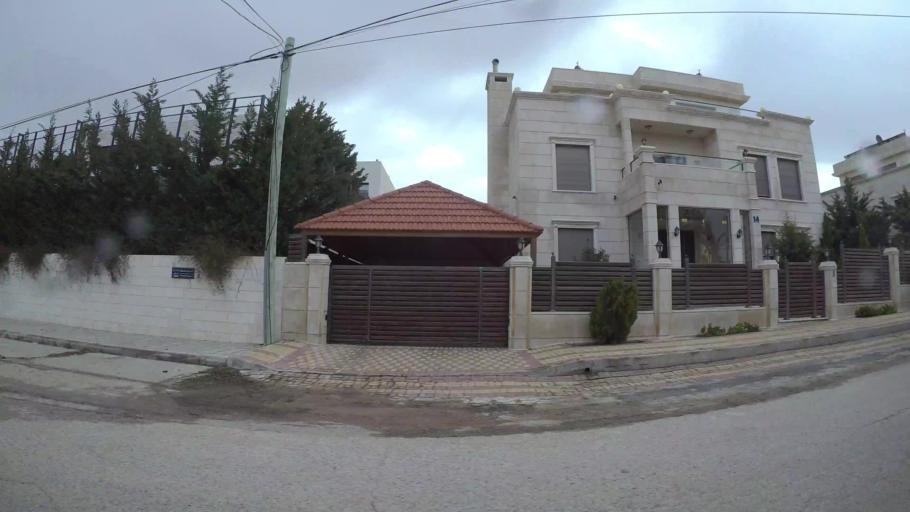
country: JO
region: Amman
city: Wadi as Sir
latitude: 31.9865
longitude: 35.8185
